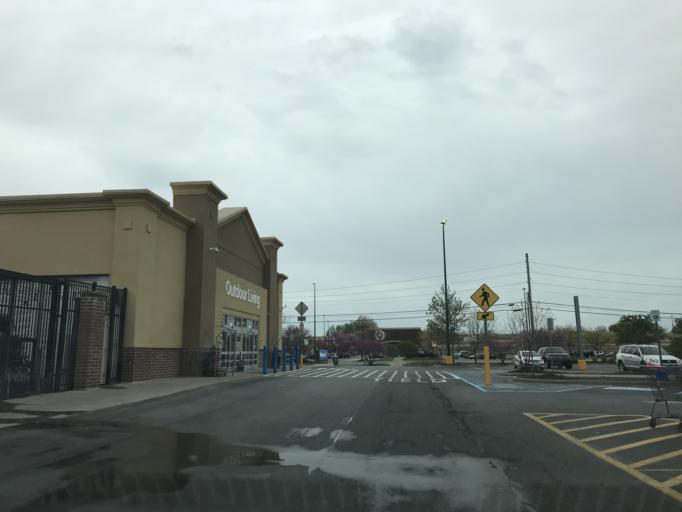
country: US
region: Kentucky
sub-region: Jefferson County
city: West Buechel
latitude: 38.1994
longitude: -85.6685
